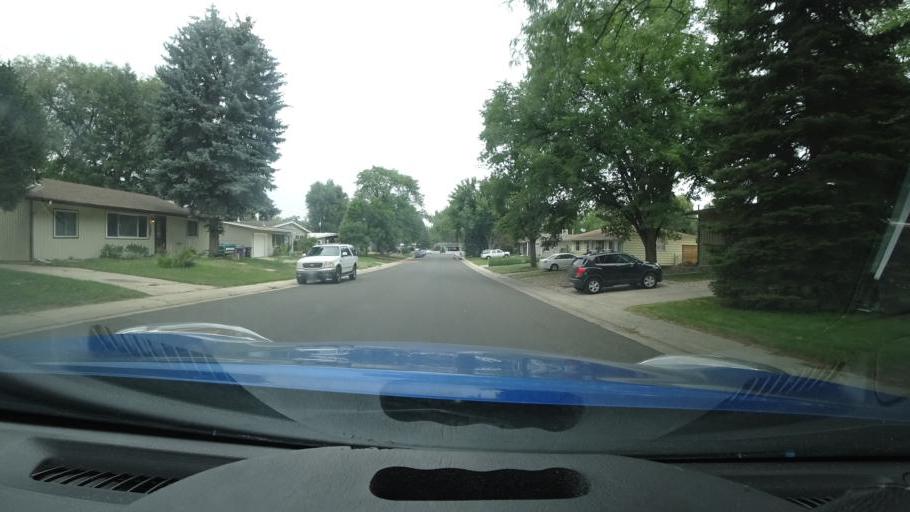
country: US
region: Colorado
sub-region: Arapahoe County
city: Glendale
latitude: 39.6909
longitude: -104.9175
